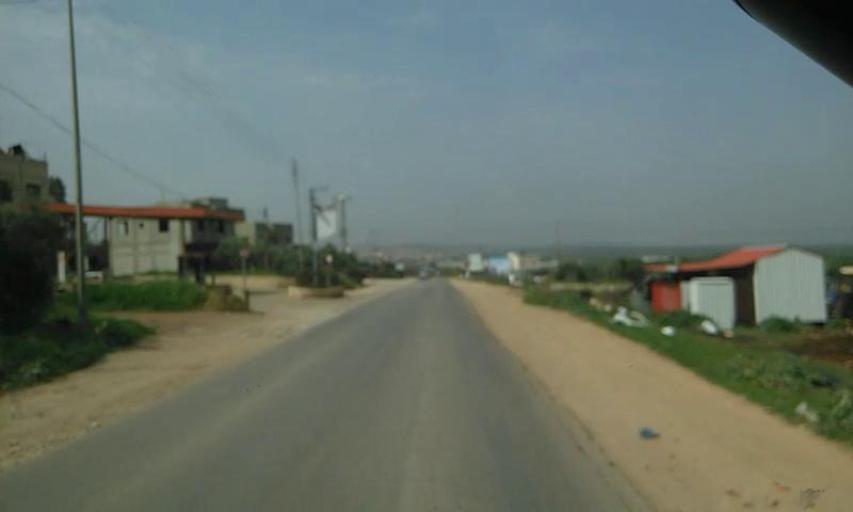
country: PS
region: West Bank
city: Kafr Dan
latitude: 32.4975
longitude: 35.2520
